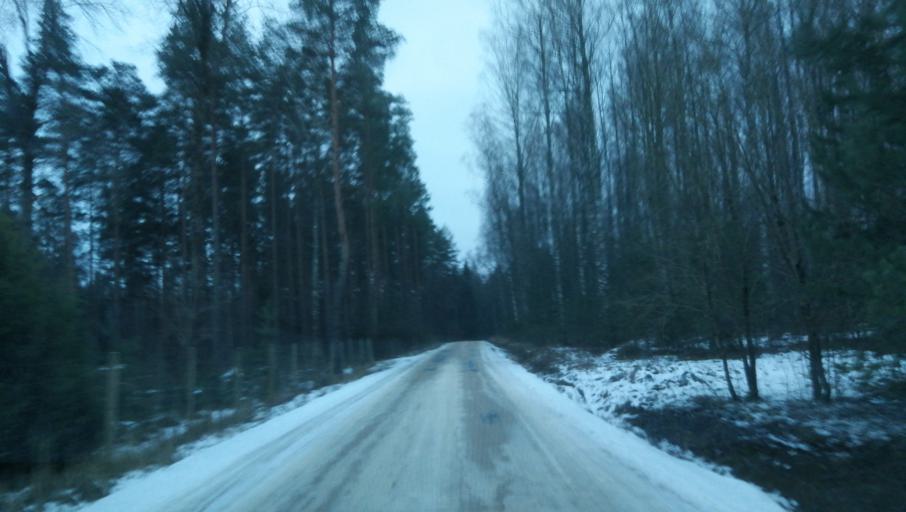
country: LV
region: Garkalne
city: Garkalne
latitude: 57.0250
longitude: 24.3861
